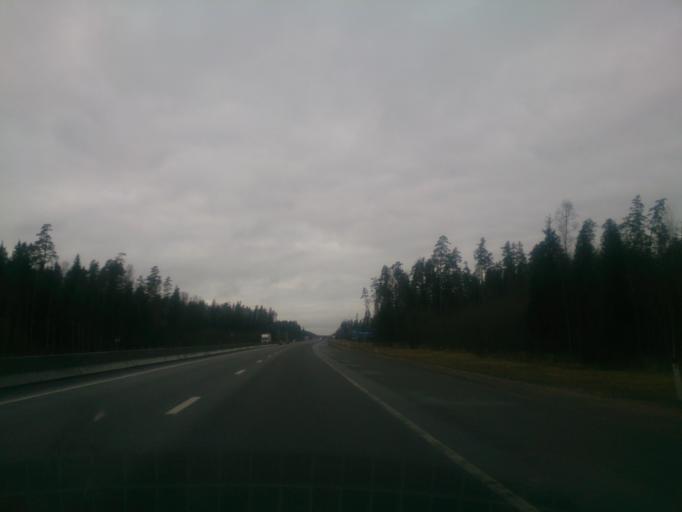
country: RU
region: Leningrad
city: Tosno
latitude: 59.4908
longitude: 30.8721
